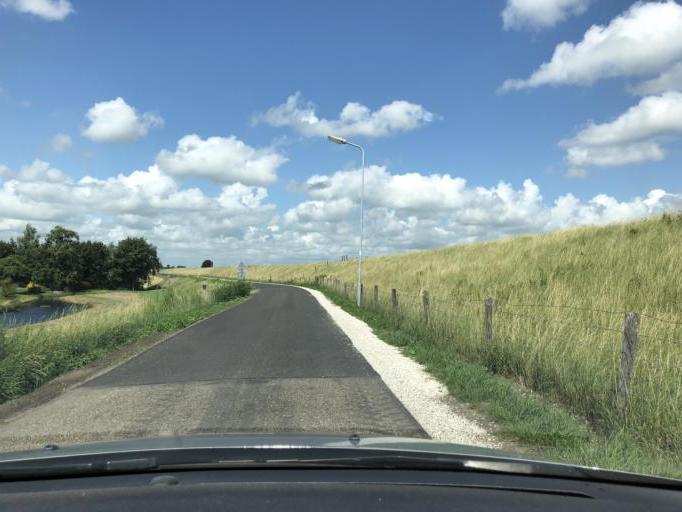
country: NL
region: North Holland
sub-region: Gemeente Hoorn
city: Hoorn
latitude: 52.6121
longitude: 5.0193
